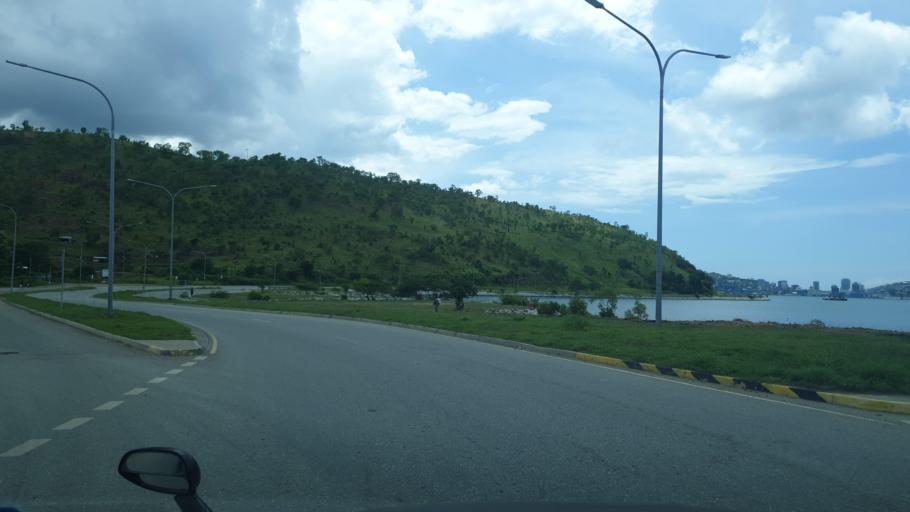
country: PG
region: National Capital
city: Port Moresby
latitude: -9.4381
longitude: 147.1385
